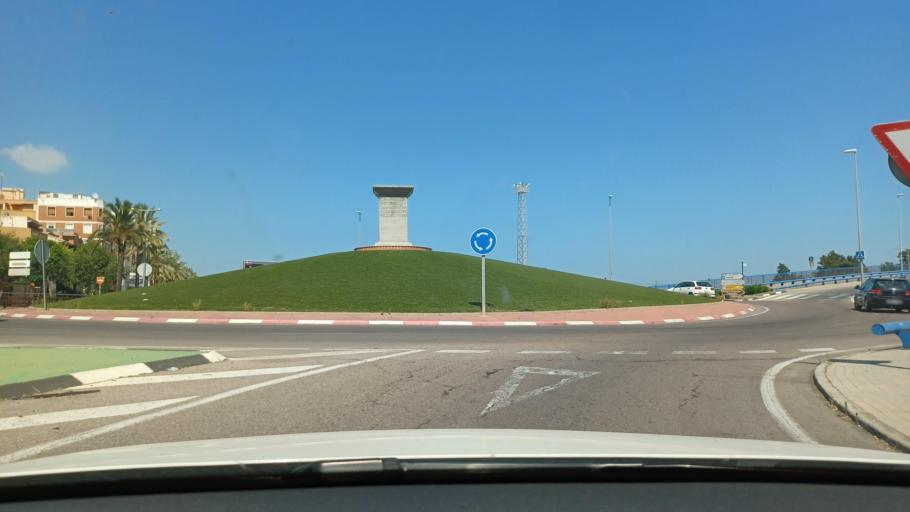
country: ES
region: Valencia
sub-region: Provincia de Valencia
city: Sagunto
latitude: 39.6742
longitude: -0.2743
